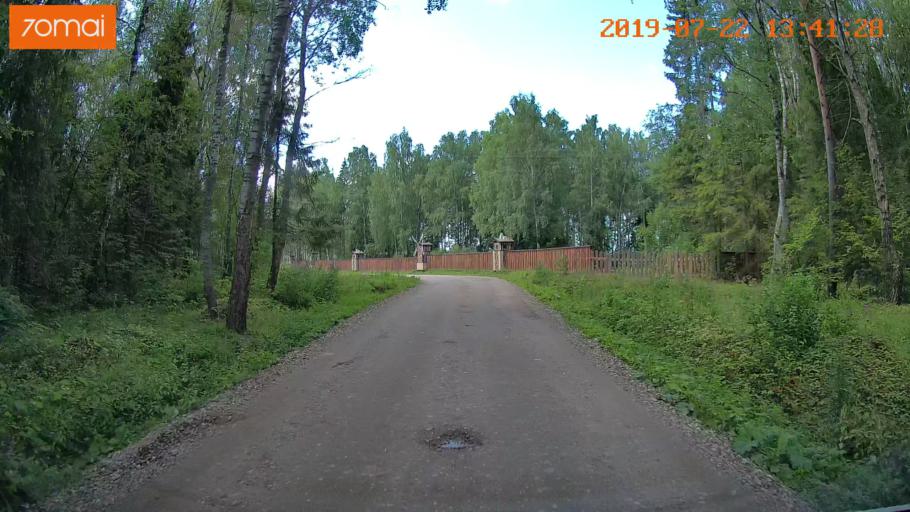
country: RU
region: Ivanovo
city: Novo-Talitsy
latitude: 57.0797
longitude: 40.8787
